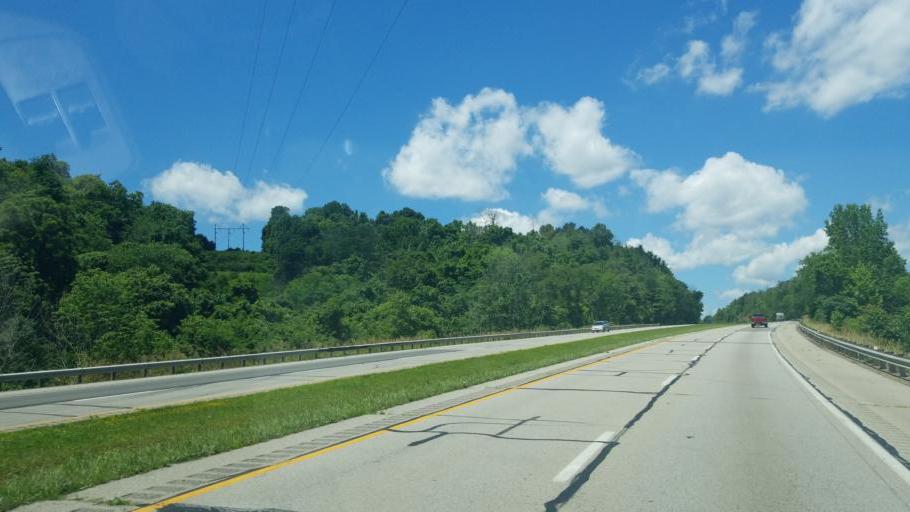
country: US
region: Ohio
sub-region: Gallia County
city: Gallipolis
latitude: 38.8404
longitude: -82.1868
